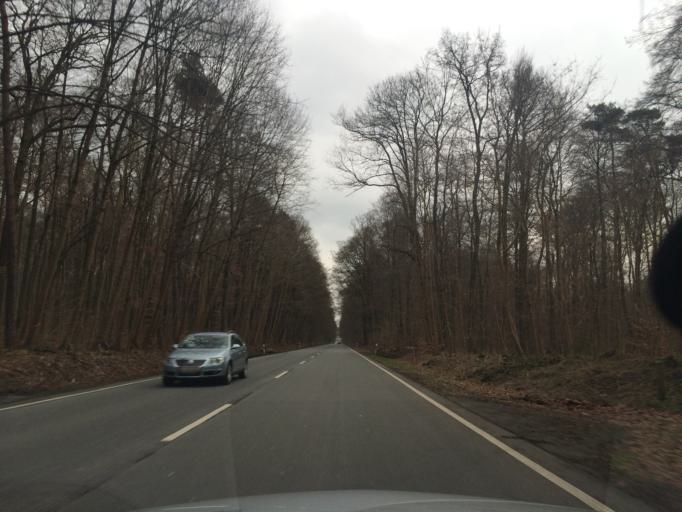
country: DE
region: Hesse
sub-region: Regierungsbezirk Darmstadt
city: Neu Isenburg
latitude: 50.0724
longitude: 8.6934
